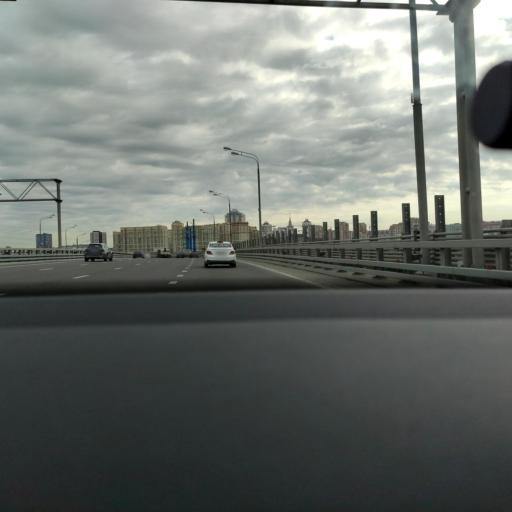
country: RU
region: Moscow
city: Amin'yevo
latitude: 55.6986
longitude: 37.4700
